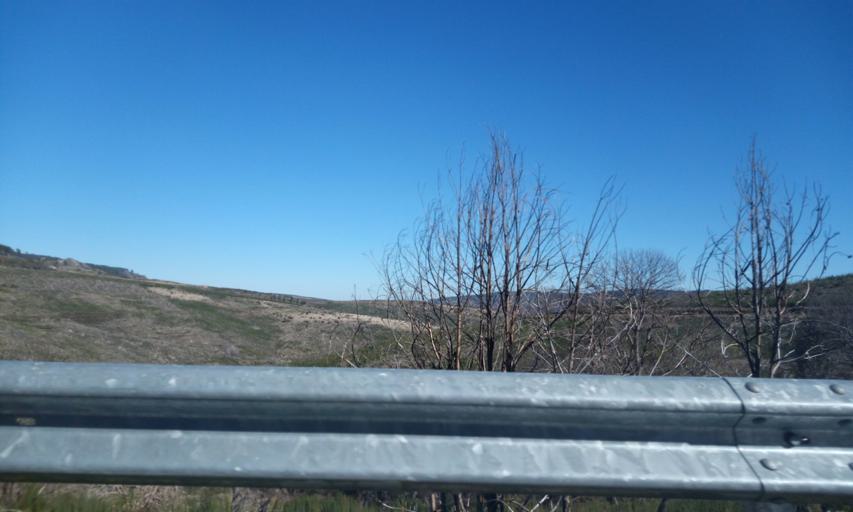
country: PT
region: Guarda
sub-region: Manteigas
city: Manteigas
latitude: 40.4653
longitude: -7.5174
